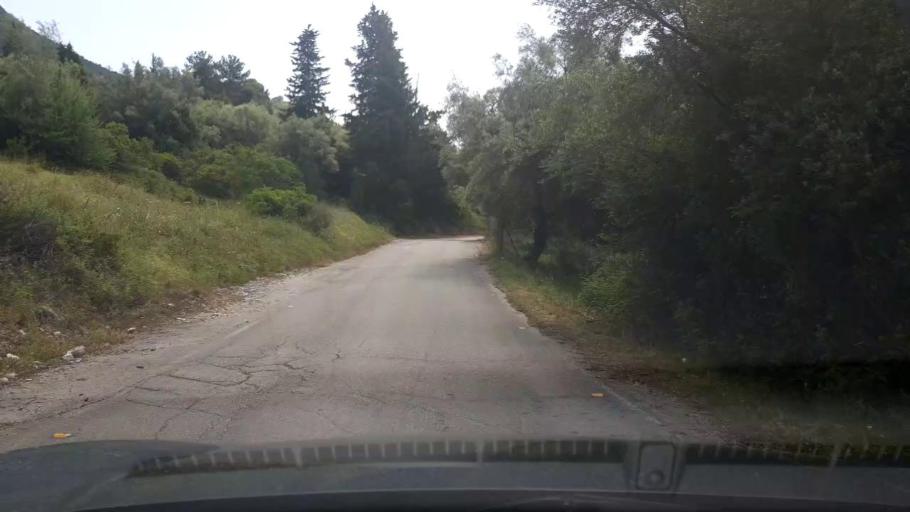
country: GR
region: Ionian Islands
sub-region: Lefkada
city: Nidri
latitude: 38.6476
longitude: 20.7034
